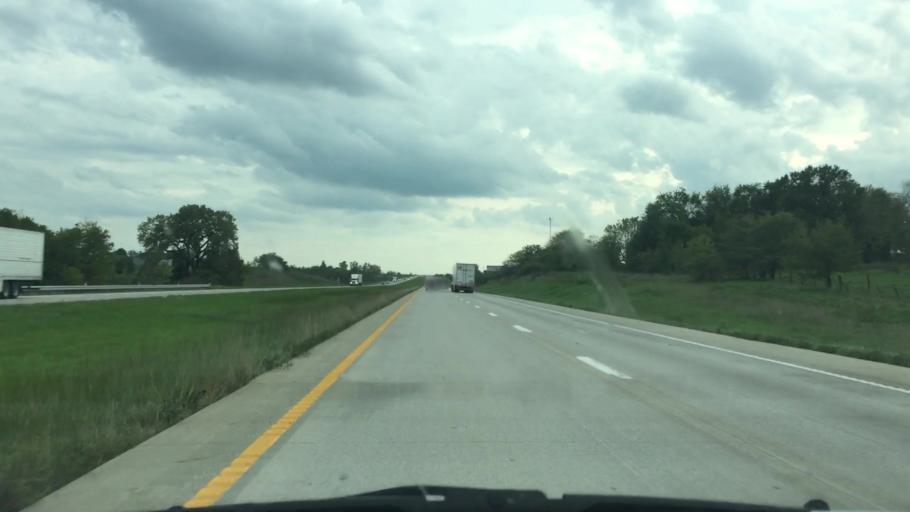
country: US
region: Missouri
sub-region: Clinton County
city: Lathrop
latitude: 39.6078
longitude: -94.2518
